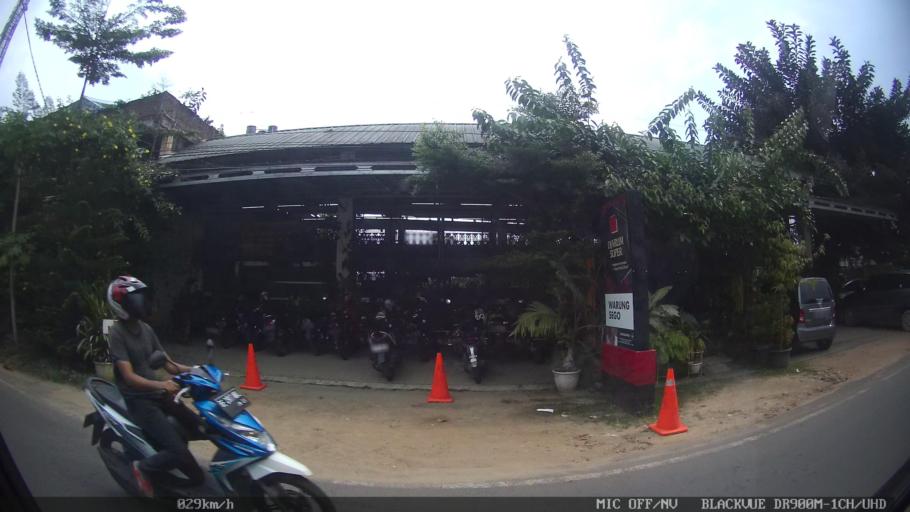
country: ID
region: Lampung
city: Bandarlampung
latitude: -5.4270
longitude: 105.2672
